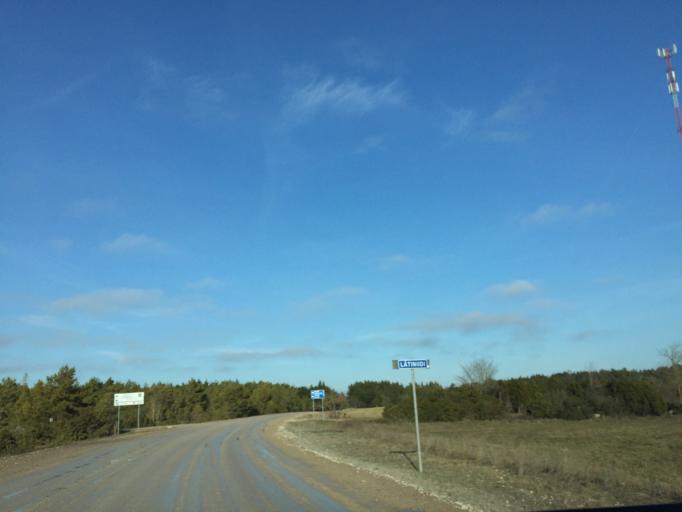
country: EE
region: Saare
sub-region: Kuressaare linn
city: Kuressaare
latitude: 58.4676
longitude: 22.0013
